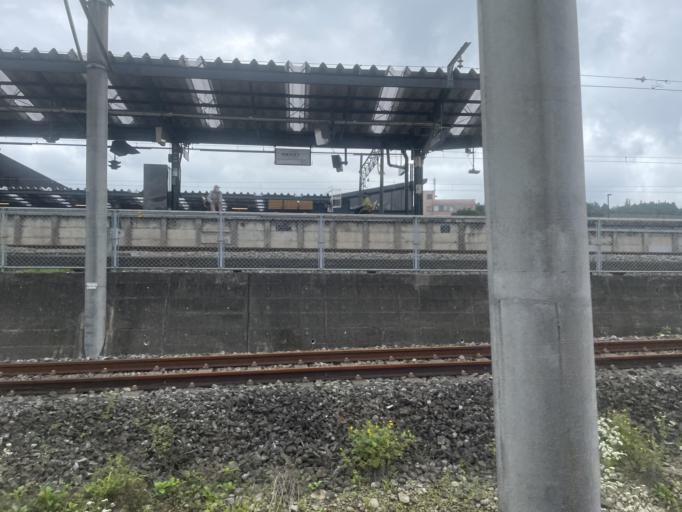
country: JP
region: Saitama
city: Chichibu
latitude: 35.9898
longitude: 139.0828
